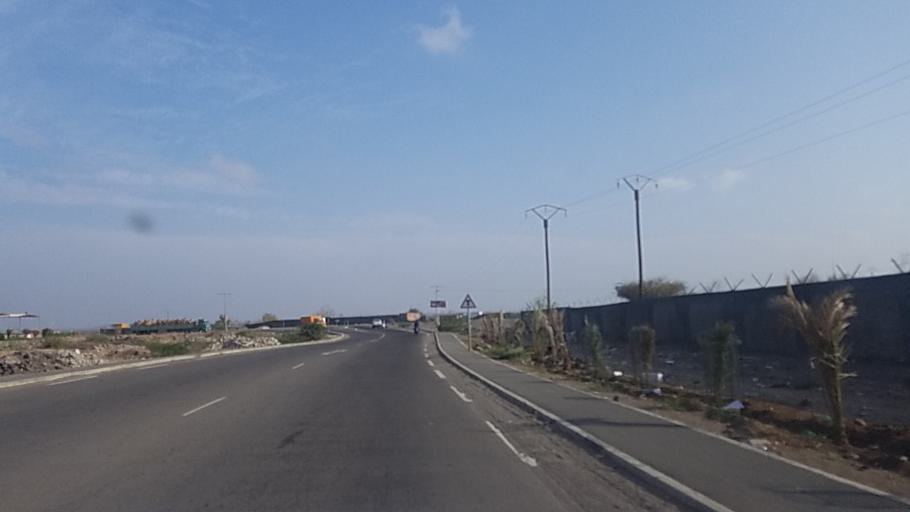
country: DJ
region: Djibouti
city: Djibouti
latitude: 11.5300
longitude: 43.1424
